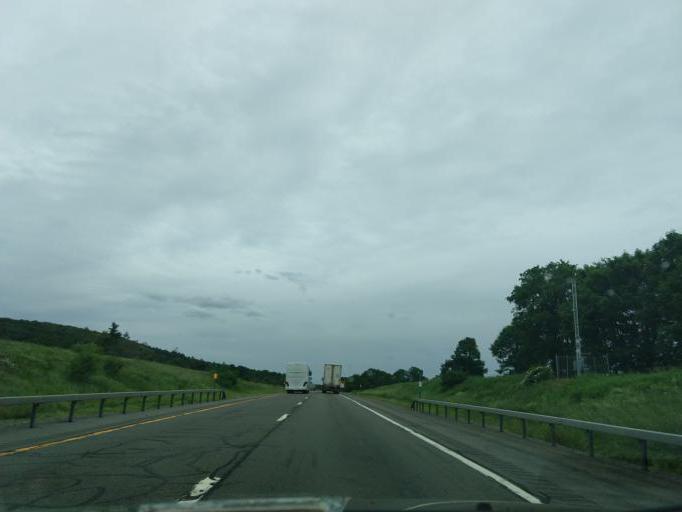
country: US
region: New York
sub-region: Chenango County
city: Lakeview
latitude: 42.4007
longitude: -76.0098
